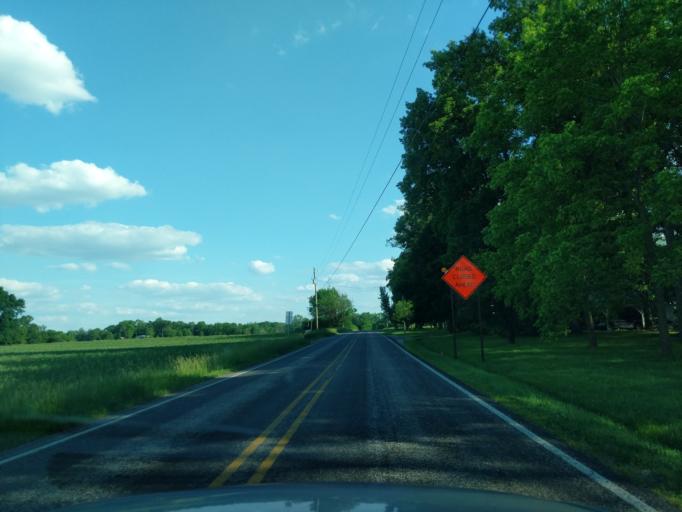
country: US
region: Indiana
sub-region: Kosciusko County
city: North Webster
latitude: 41.3038
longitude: -85.6433
